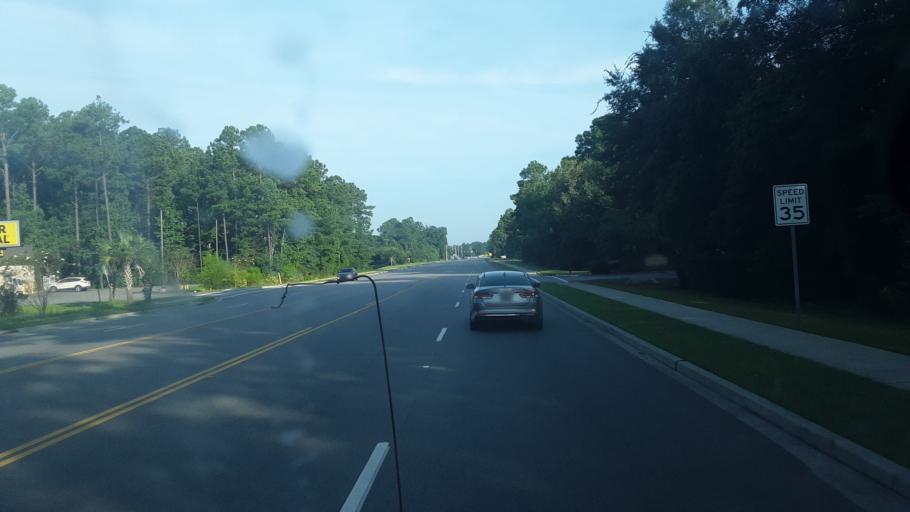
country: US
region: South Carolina
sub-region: Horry County
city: Myrtle Beach
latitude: 33.7614
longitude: -78.8600
